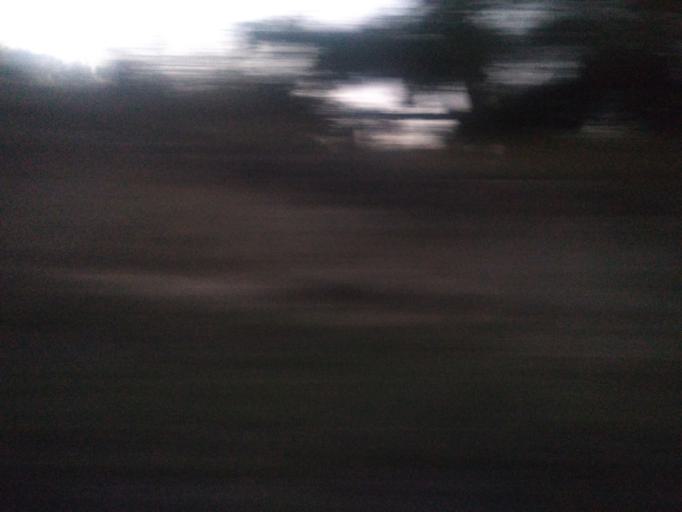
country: MX
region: Puebla
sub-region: Oriental
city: San Antonio Virreyes
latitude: 19.4134
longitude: -97.6473
